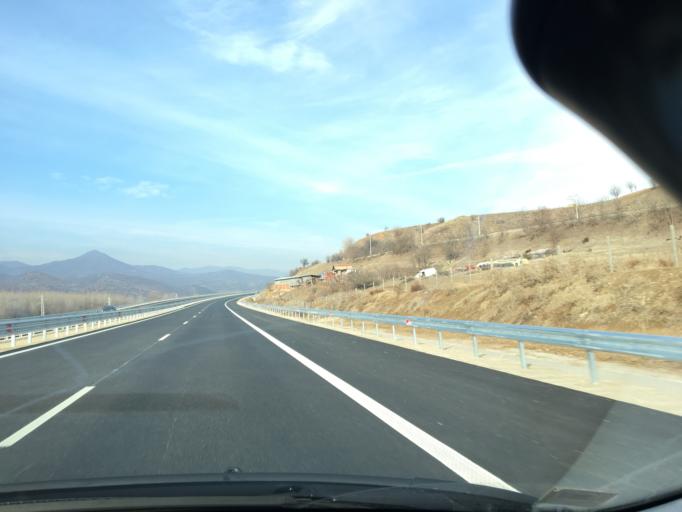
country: BG
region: Blagoevgrad
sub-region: Obshtina Sandanski
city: Sandanski
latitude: 41.5565
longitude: 23.2458
